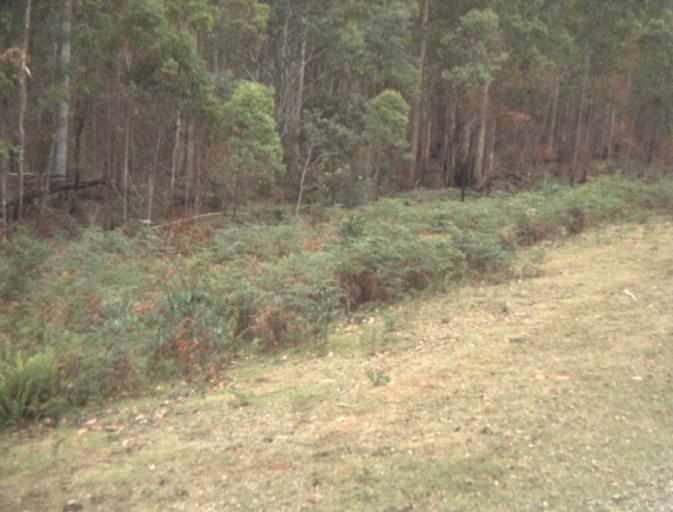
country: AU
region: Tasmania
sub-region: Dorset
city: Scottsdale
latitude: -41.4294
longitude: 147.5139
